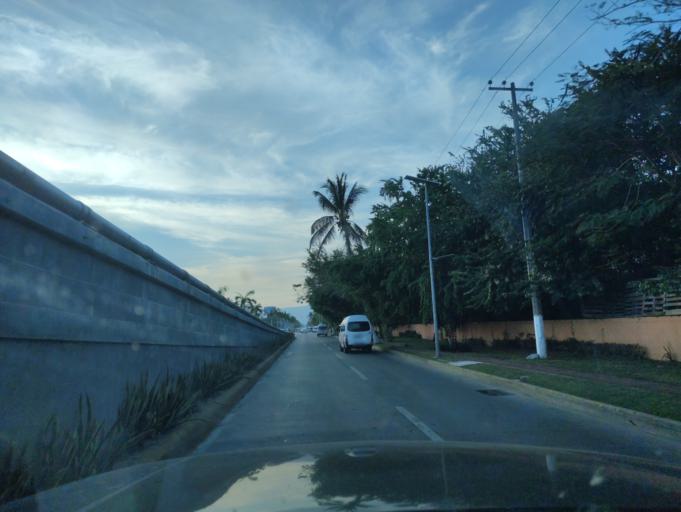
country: MX
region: Guerrero
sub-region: Acapulco de Juarez
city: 10 de Abril
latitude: 16.7733
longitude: -99.7749
